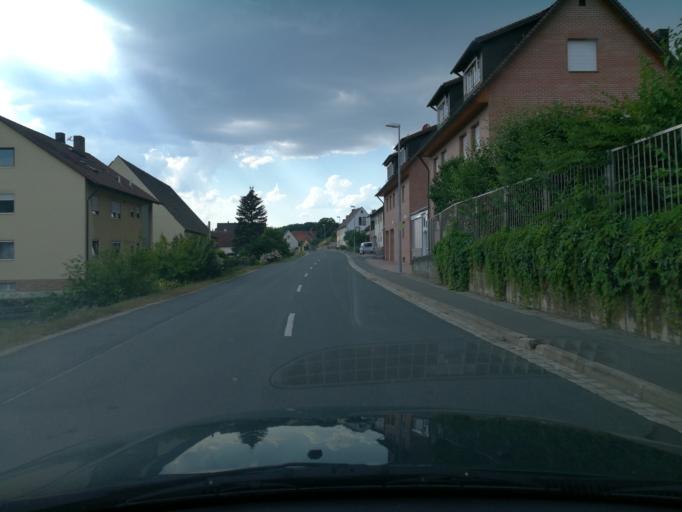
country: DE
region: Bavaria
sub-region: Regierungsbezirk Mittelfranken
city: Grosshabersdorf
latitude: 49.4086
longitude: 10.7664
